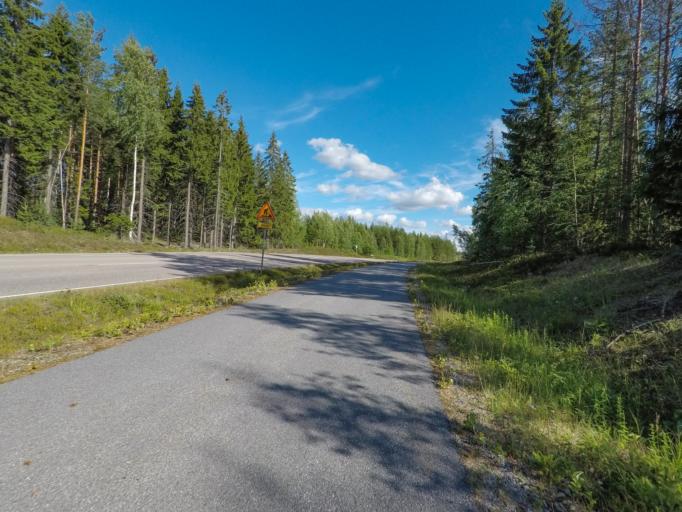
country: FI
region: South Karelia
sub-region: Lappeenranta
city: Joutseno
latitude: 61.1525
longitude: 28.6125
